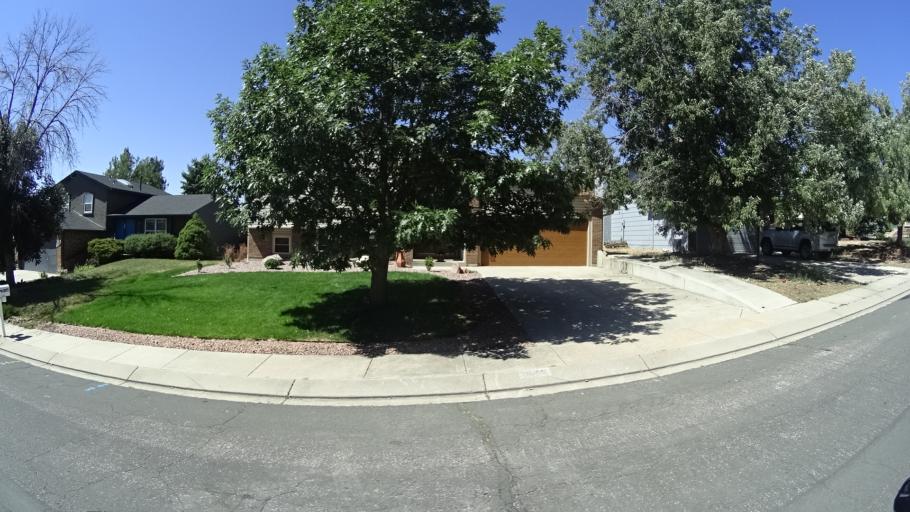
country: US
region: Colorado
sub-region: El Paso County
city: Black Forest
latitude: 38.9440
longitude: -104.7583
